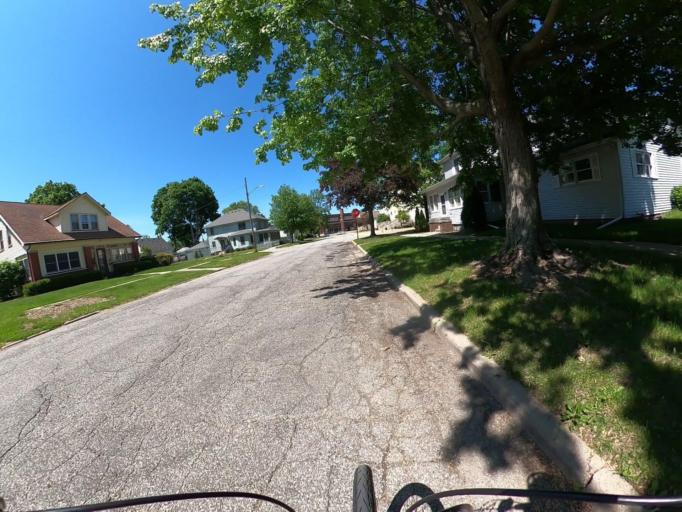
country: US
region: Indiana
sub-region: LaPorte County
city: LaPorte
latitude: 41.6053
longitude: -86.7216
